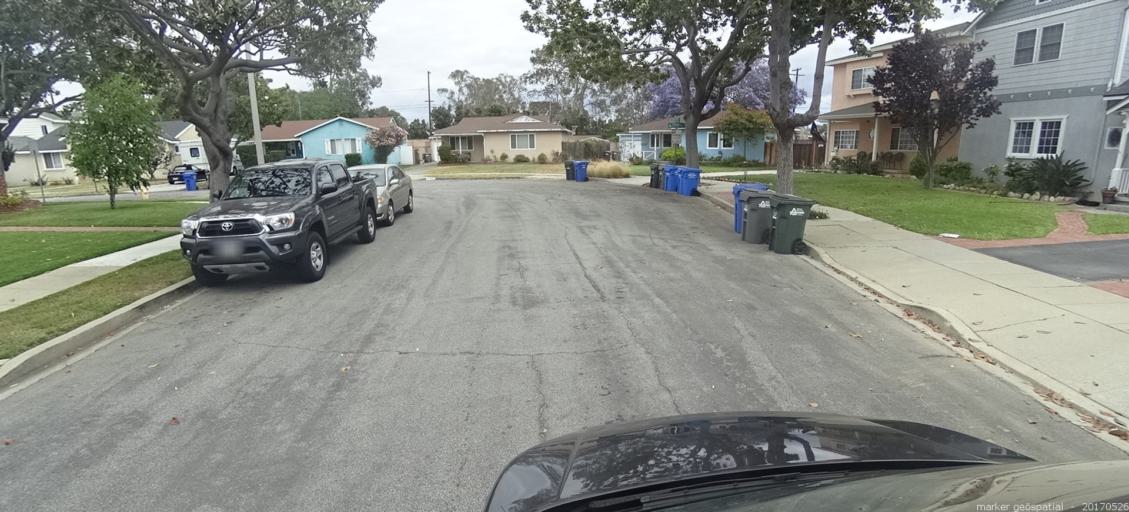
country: US
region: California
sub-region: Los Angeles County
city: Lawndale
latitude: 33.8640
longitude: -118.3598
